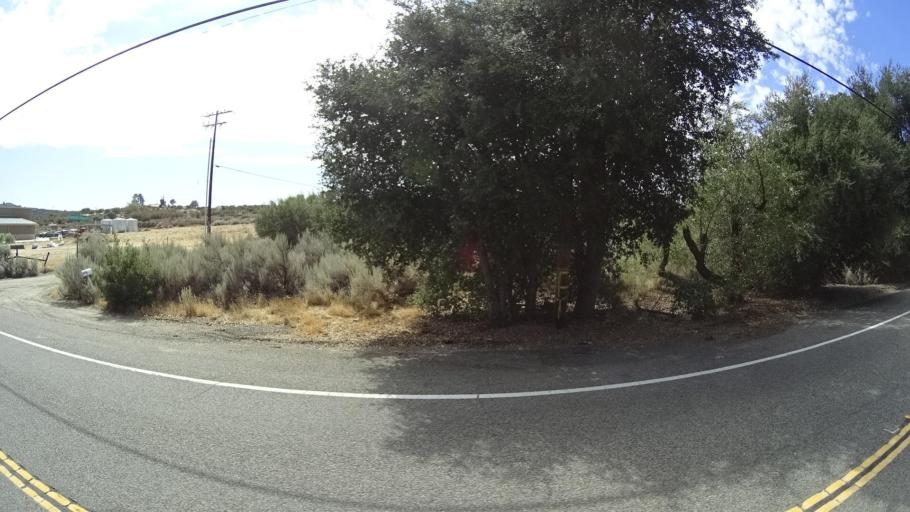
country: US
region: California
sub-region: San Diego County
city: Campo
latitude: 32.6732
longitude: -116.2905
